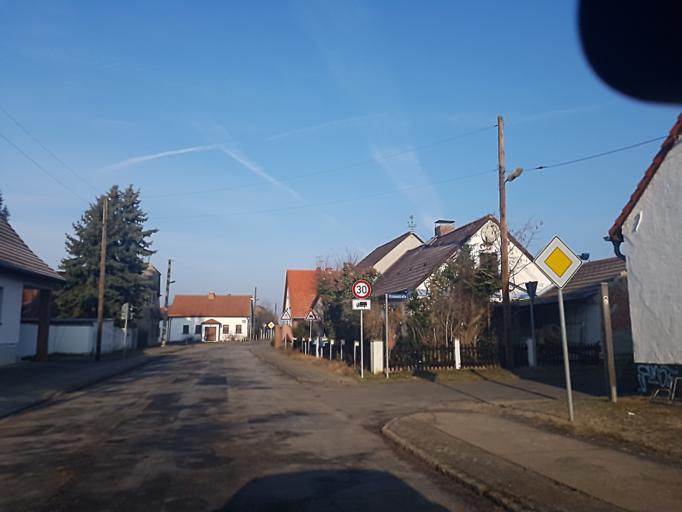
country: DE
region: Brandenburg
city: Wollin
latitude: 52.2487
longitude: 12.4842
